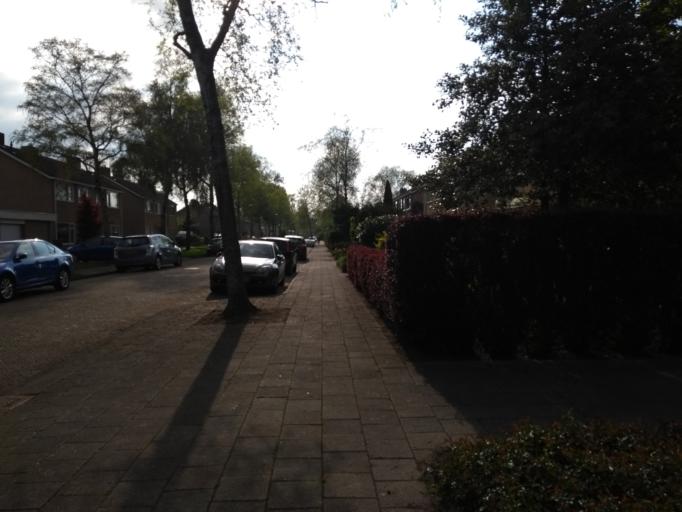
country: NL
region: Friesland
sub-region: Gemeente Smallingerland
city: Drachten
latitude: 53.1033
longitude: 6.1131
